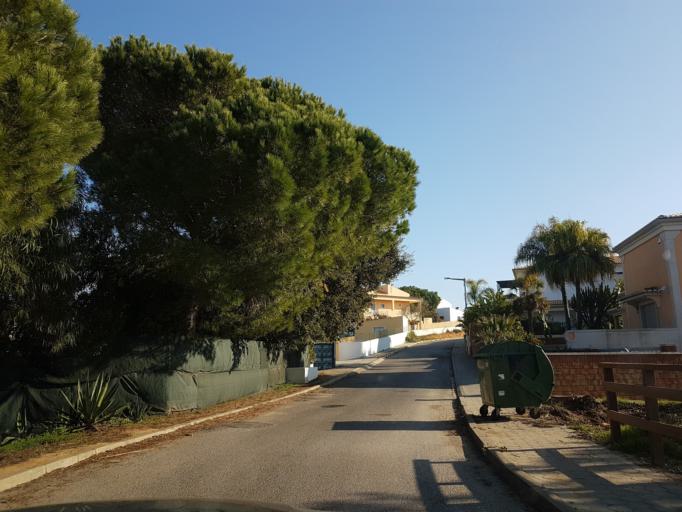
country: PT
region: Faro
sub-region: Albufeira
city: Albufeira
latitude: 37.0945
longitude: -8.2013
